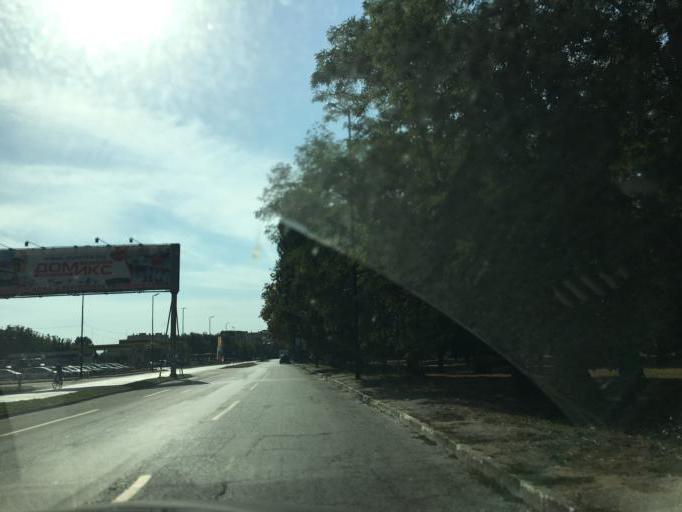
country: BG
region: Pazardzhik
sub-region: Obshtina Pazardzhik
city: Pazardzhik
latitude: 42.2090
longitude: 24.3259
